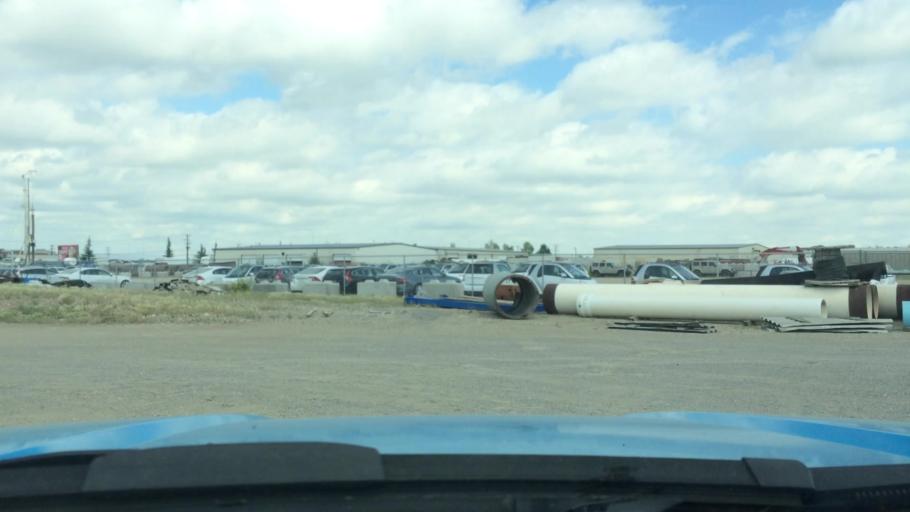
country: CA
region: Alberta
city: Airdrie
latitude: 51.2928
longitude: -113.9874
